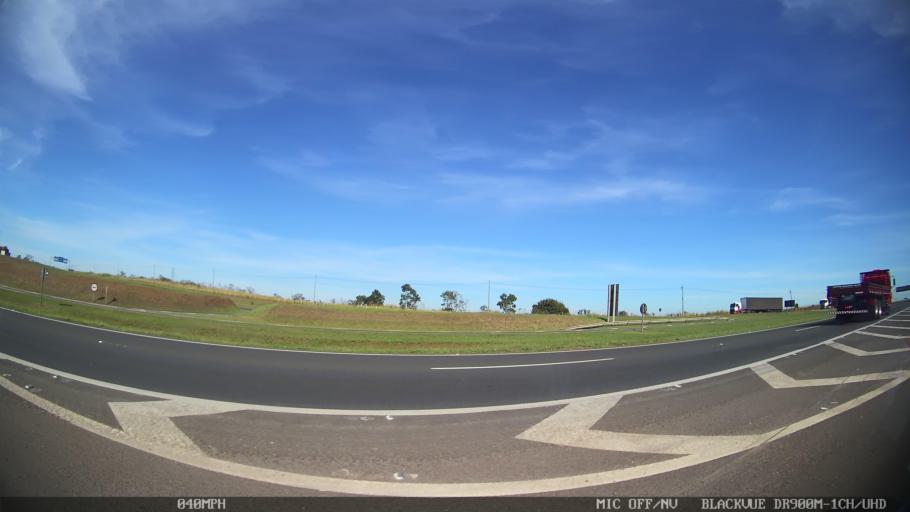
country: BR
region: Sao Paulo
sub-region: Cordeiropolis
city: Cordeiropolis
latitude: -22.5017
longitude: -47.4005
